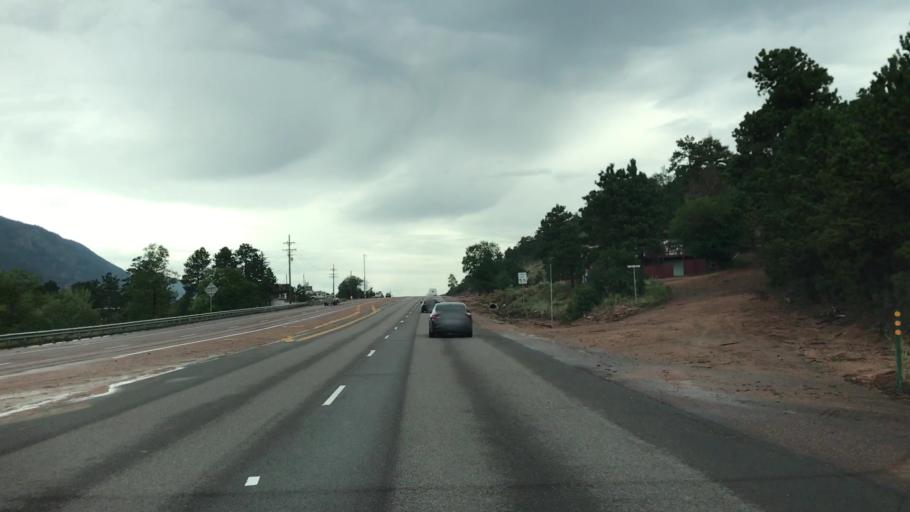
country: US
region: Colorado
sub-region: El Paso County
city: Cascade-Chipita Park
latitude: 38.9106
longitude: -104.9749
